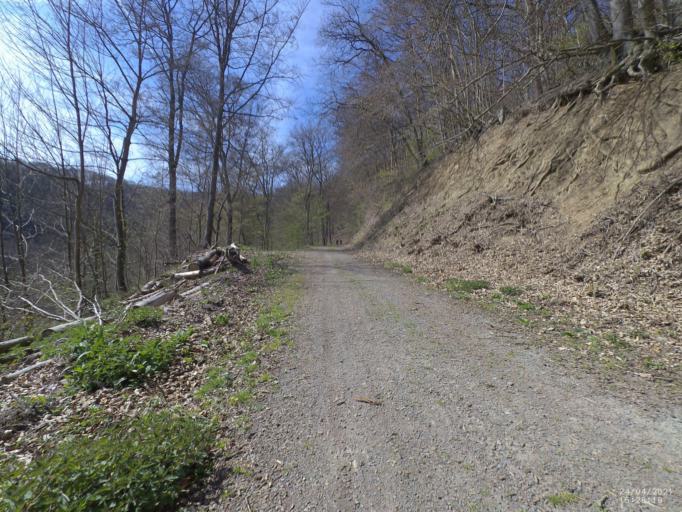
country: DE
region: Rheinland-Pfalz
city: Stromberg
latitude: 50.4507
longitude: 7.5813
